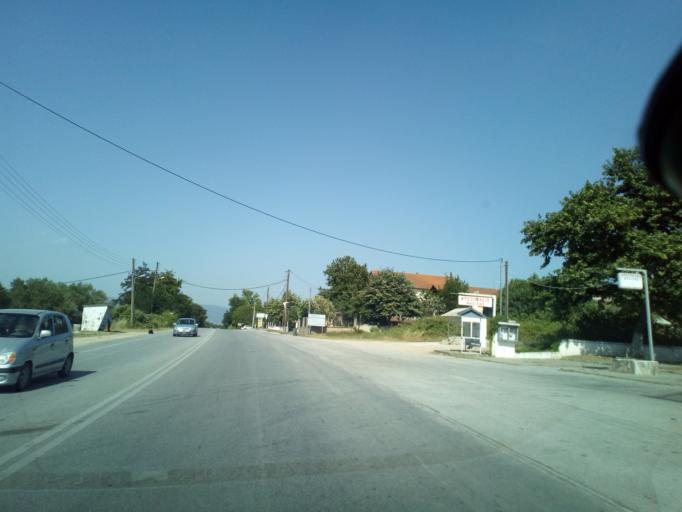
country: GR
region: Central Macedonia
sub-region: Nomos Thessalonikis
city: Gerakarou
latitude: 40.6533
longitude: 23.3034
